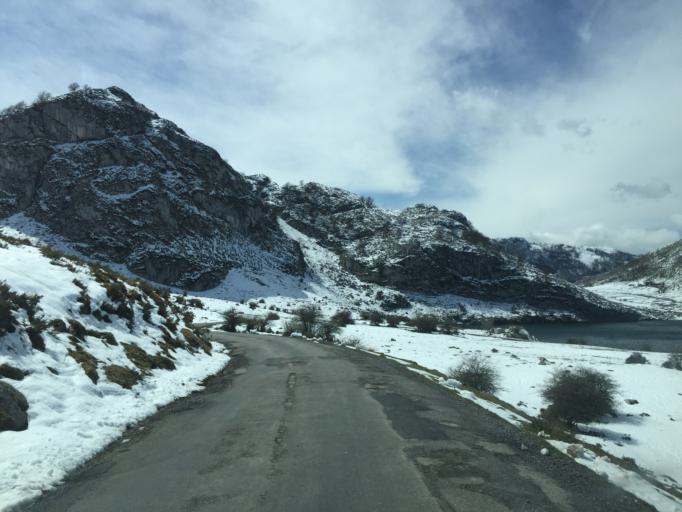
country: ES
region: Asturias
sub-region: Province of Asturias
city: Amieva
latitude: 43.2734
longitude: -4.9856
